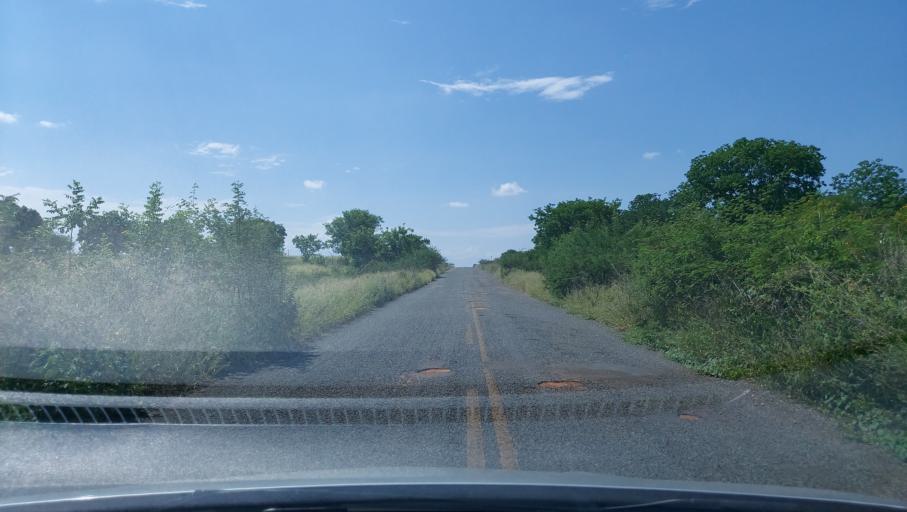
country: BR
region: Bahia
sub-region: Oliveira Dos Brejinhos
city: Beira Rio
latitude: -12.1604
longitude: -42.5499
